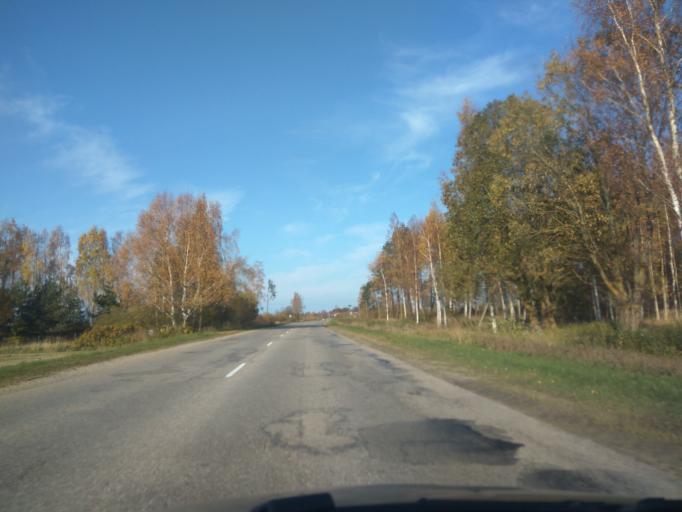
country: LV
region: Ventspils
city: Ventspils
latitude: 57.2936
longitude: 21.5638
